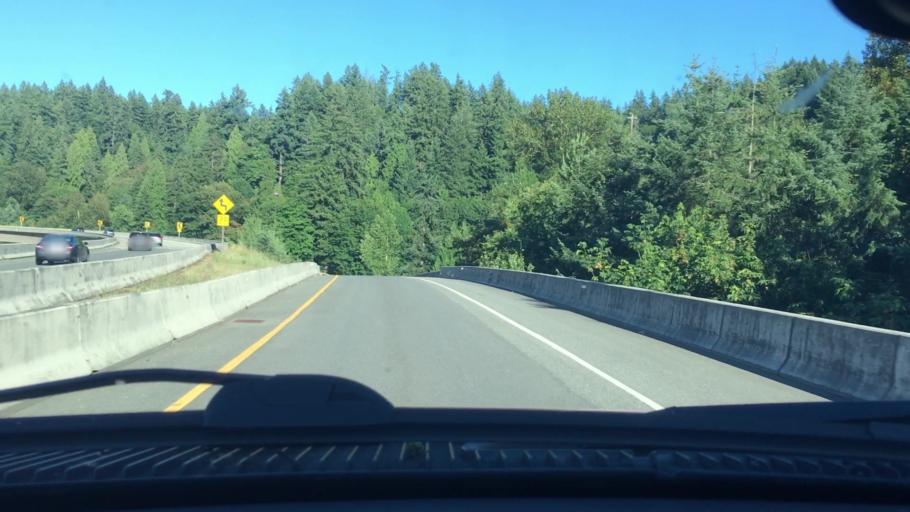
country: US
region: Washington
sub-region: King County
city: Issaquah
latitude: 47.5316
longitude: -122.0265
